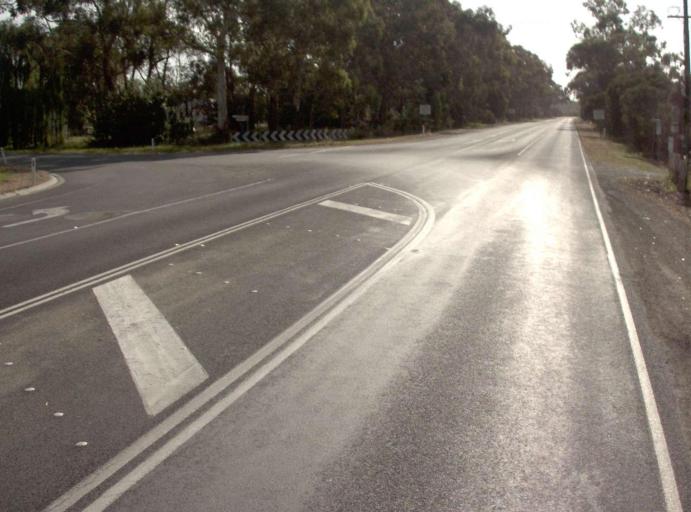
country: AU
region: Victoria
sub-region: Cardinia
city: Bunyip
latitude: -38.0816
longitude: 145.7788
